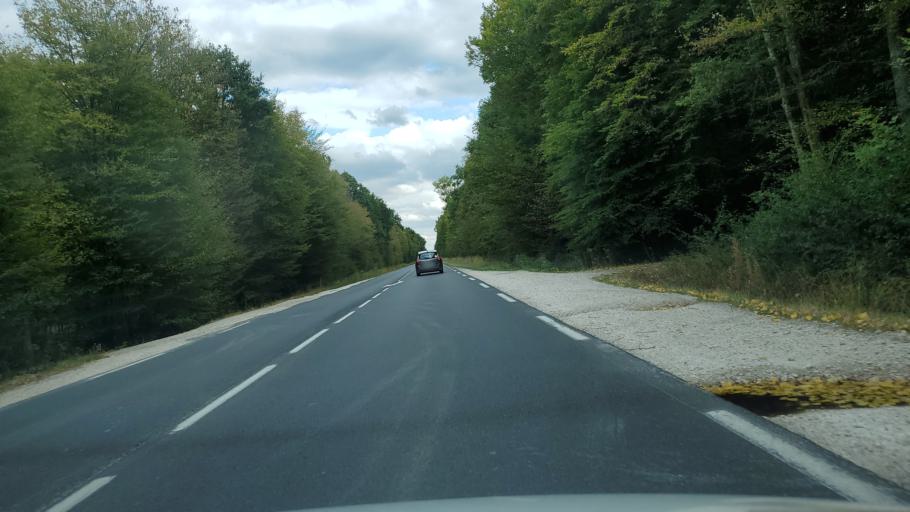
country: FR
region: Ile-de-France
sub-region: Departement de Seine-et-Marne
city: Villeneuve-le-Comte
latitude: 48.8027
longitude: 2.8478
